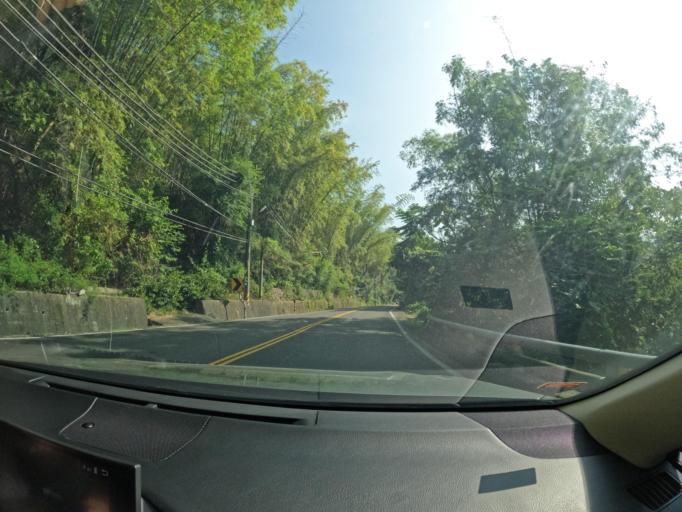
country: TW
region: Taiwan
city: Yujing
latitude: 23.0628
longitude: 120.5630
